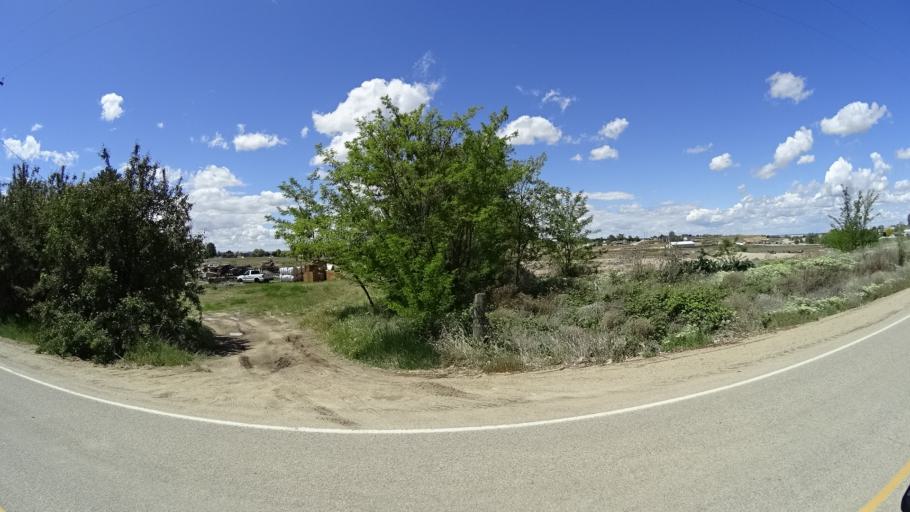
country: US
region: Idaho
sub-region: Ada County
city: Meridian
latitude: 43.5830
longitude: -116.4735
